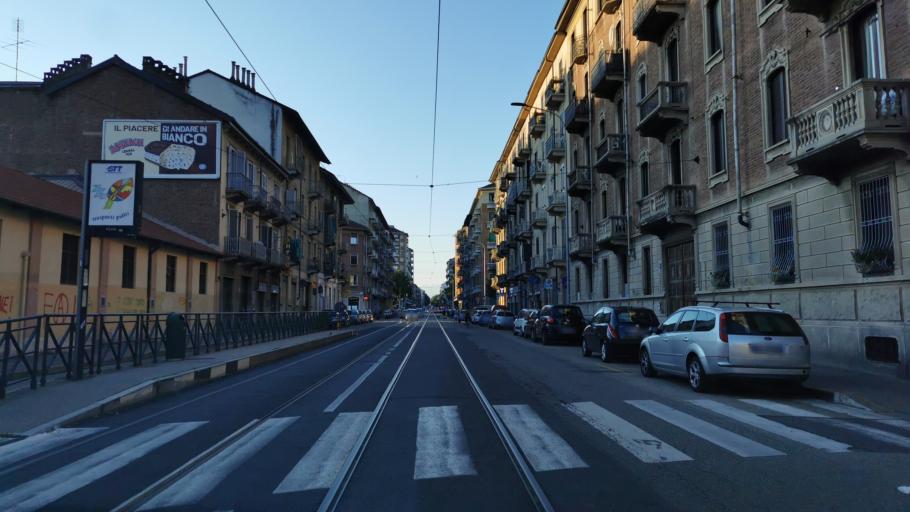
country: IT
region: Piedmont
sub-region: Provincia di Torino
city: Turin
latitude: 45.0825
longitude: 7.6929
